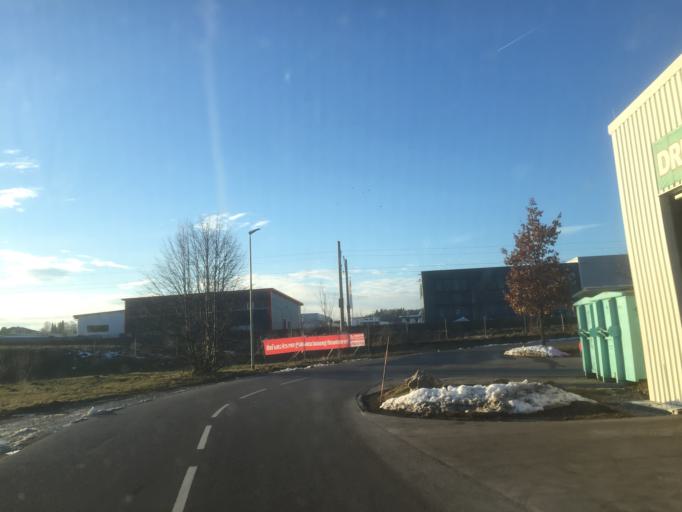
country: DE
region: Bavaria
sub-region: Upper Bavaria
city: Vachendorf
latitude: 47.8529
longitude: 12.6282
